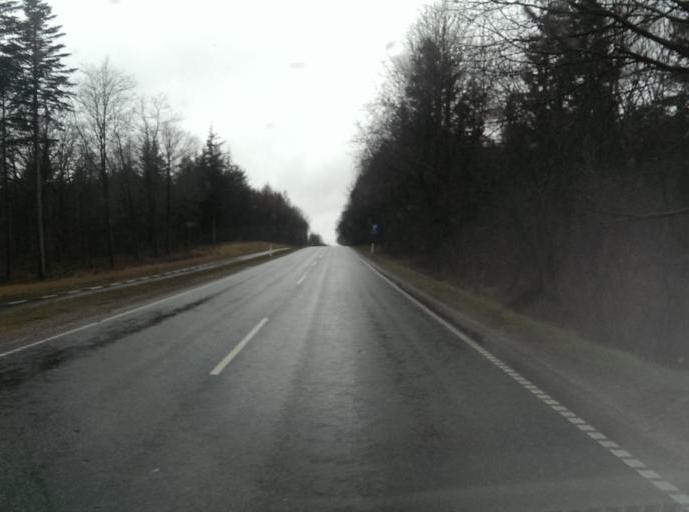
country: DK
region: Central Jutland
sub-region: Ringkobing-Skjern Kommune
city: Skjern
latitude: 55.9866
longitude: 8.4558
